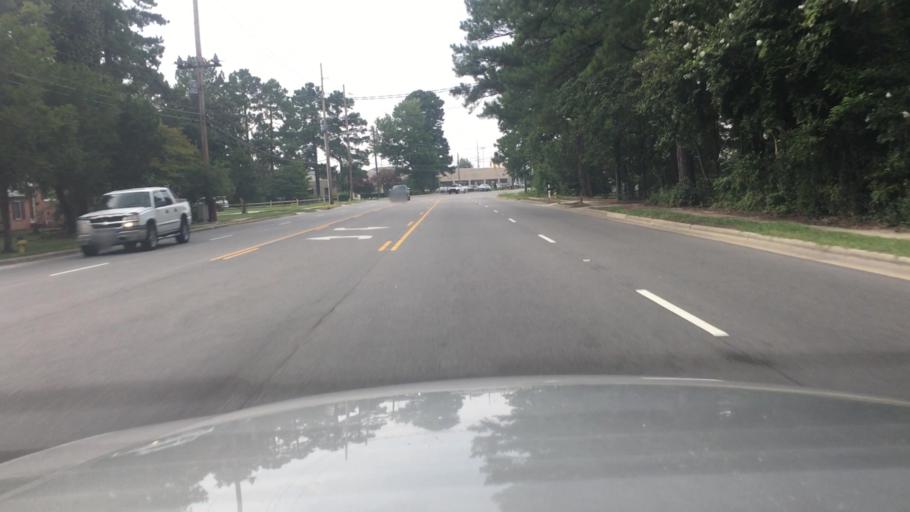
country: US
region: North Carolina
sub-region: Cumberland County
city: Fayetteville
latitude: 35.0633
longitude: -78.9504
